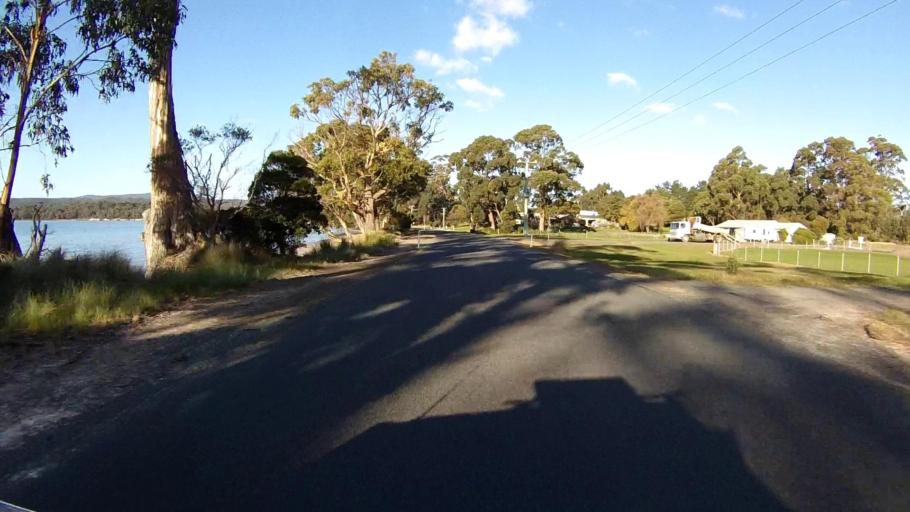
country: AU
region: Tasmania
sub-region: Clarence
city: Sandford
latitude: -43.1576
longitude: 147.8501
